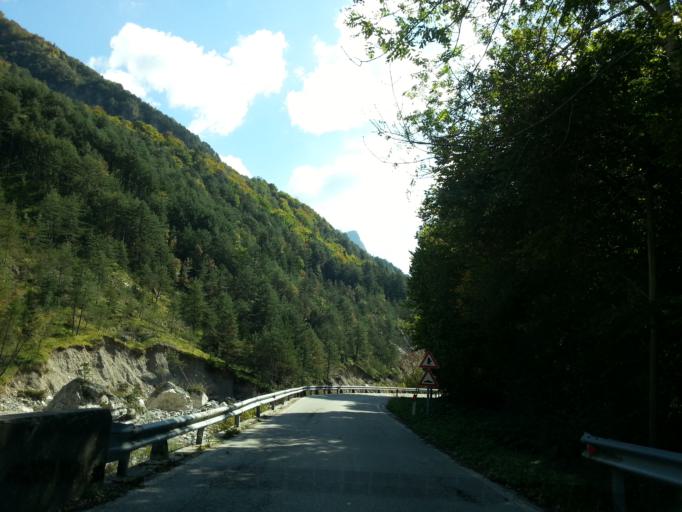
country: IT
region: Friuli Venezia Giulia
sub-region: Provincia di Udine
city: Moggio Udinese
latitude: 46.4801
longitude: 13.1893
